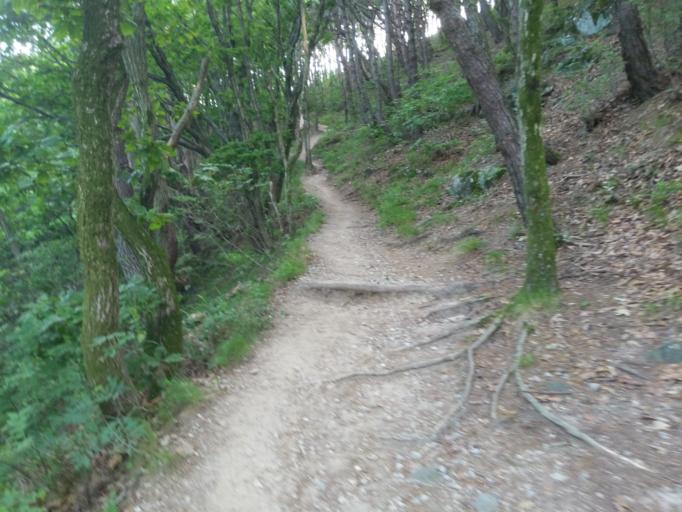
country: KR
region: Daegu
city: Hwawon
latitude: 35.7855
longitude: 128.5467
